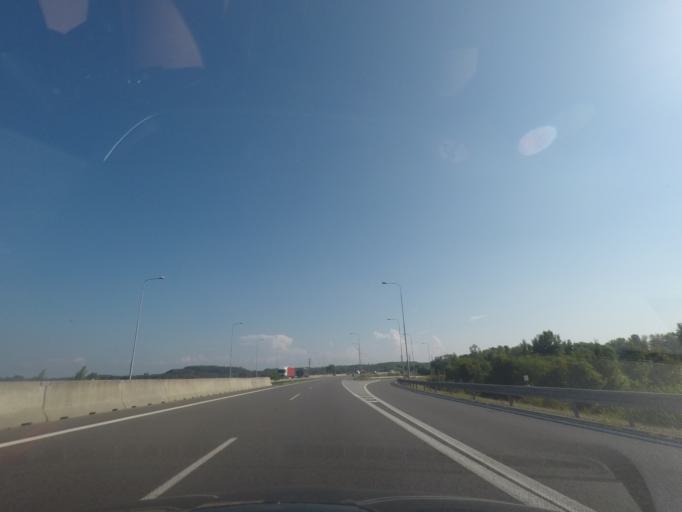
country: PL
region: Silesian Voivodeship
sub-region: Powiat raciborski
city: Chalupki
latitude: 49.8844
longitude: 18.3059
